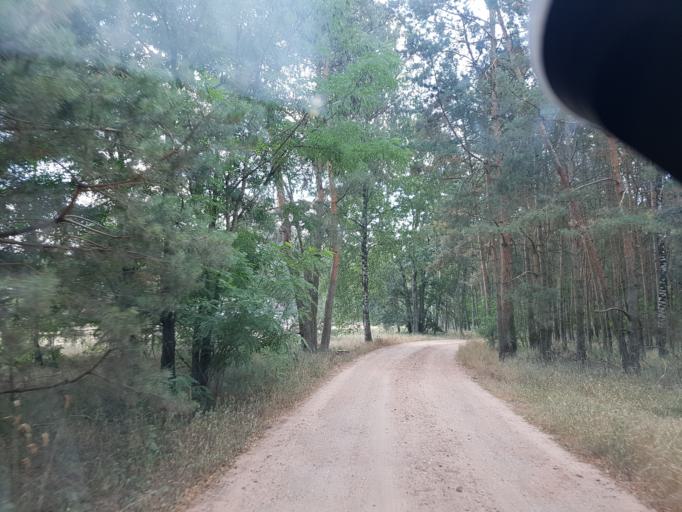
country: DE
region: Brandenburg
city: Heinersbruck
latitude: 51.7150
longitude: 14.4483
